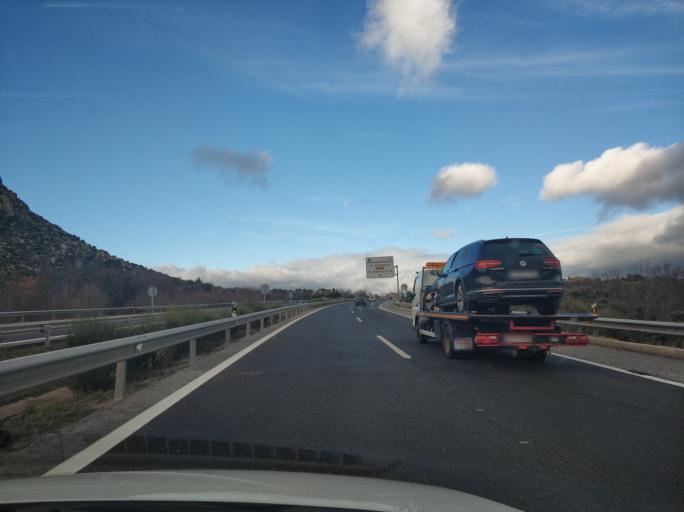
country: ES
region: Madrid
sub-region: Provincia de Madrid
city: La Cabrera
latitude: 40.8701
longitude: -3.6049
